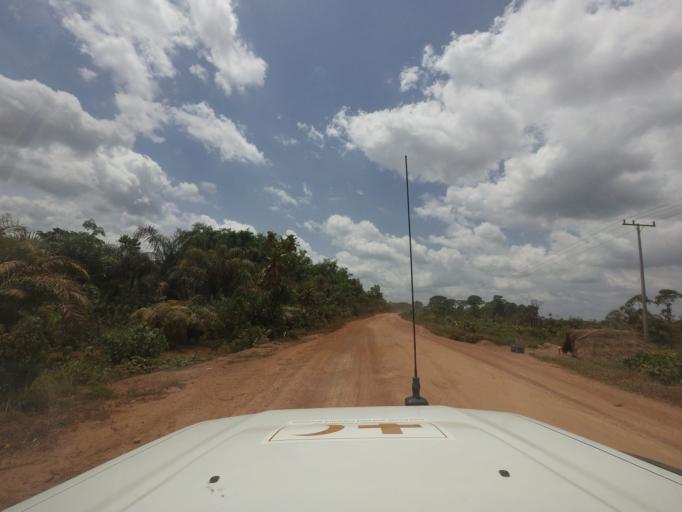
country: LR
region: Nimba
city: Sanniquellie
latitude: 7.2340
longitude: -8.9594
